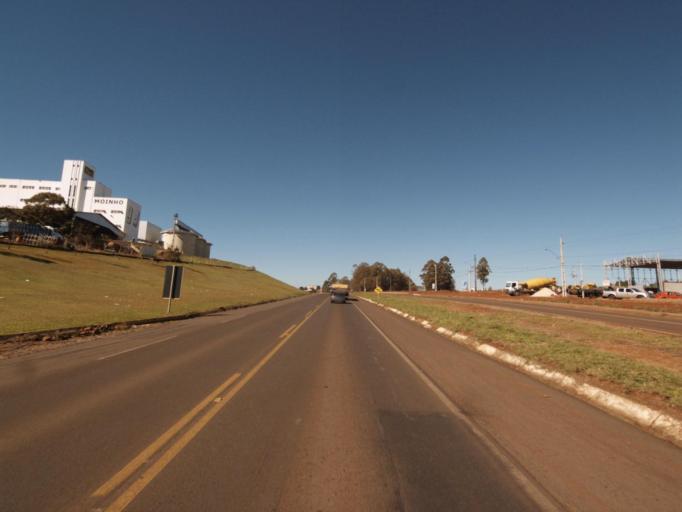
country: BR
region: Santa Catarina
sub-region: Chapeco
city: Chapeco
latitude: -26.8332
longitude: -52.9932
